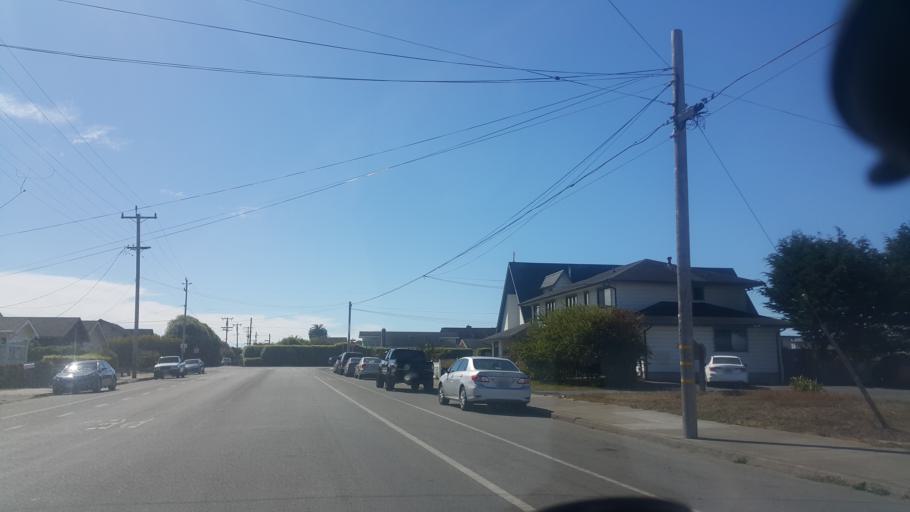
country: US
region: California
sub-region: Mendocino County
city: Fort Bragg
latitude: 39.4400
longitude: -123.7981
